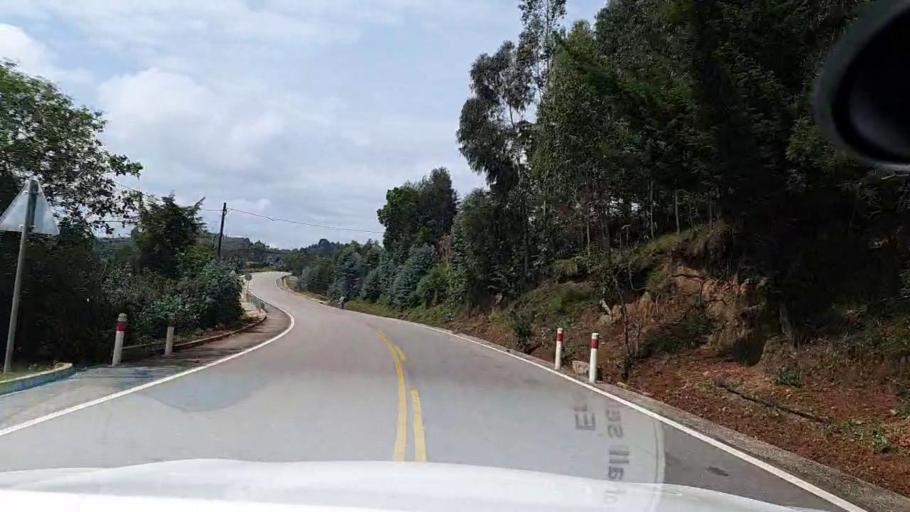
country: RW
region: Southern Province
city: Nzega
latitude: -2.4858
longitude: 29.5143
